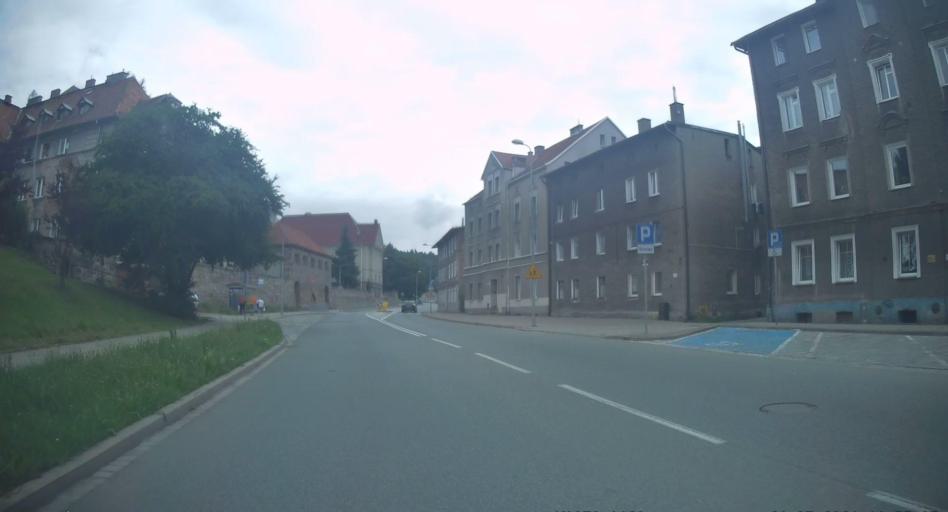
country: PL
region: Lower Silesian Voivodeship
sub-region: Powiat walbrzyski
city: Walbrzych
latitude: 50.7789
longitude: 16.2959
